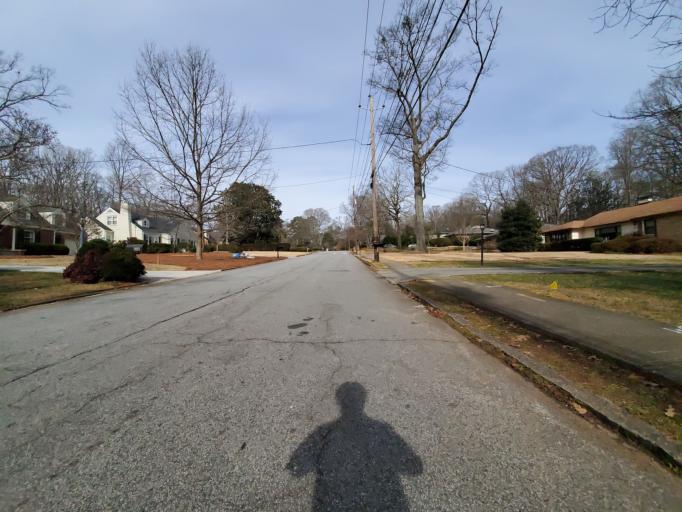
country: US
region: Georgia
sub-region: DeKalb County
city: North Decatur
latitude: 33.7747
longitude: -84.3162
